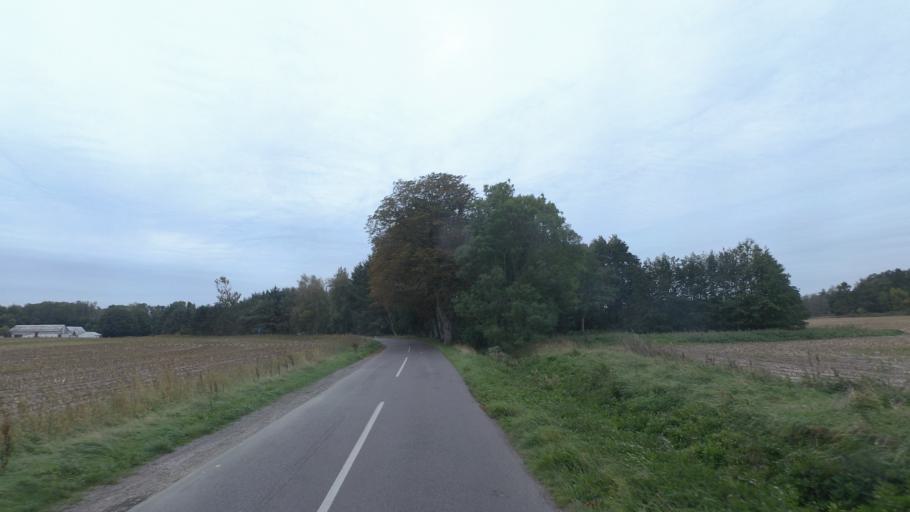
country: DK
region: Capital Region
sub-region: Bornholm Kommune
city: Akirkeby
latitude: 55.0077
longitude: 14.9914
